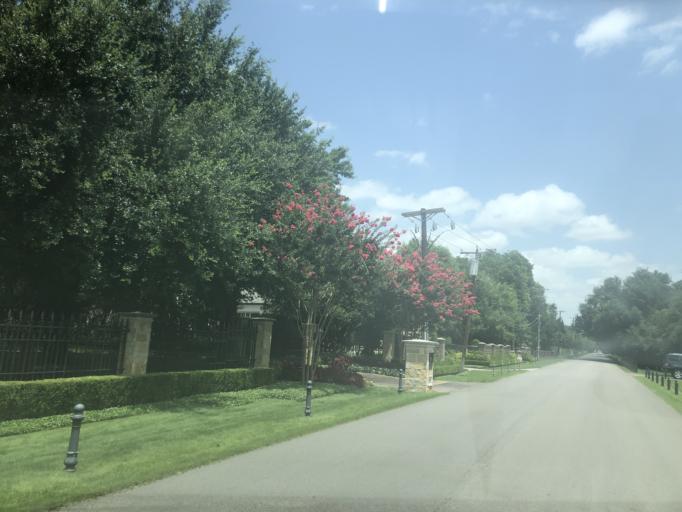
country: US
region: Texas
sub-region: Dallas County
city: University Park
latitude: 32.8873
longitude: -96.8236
